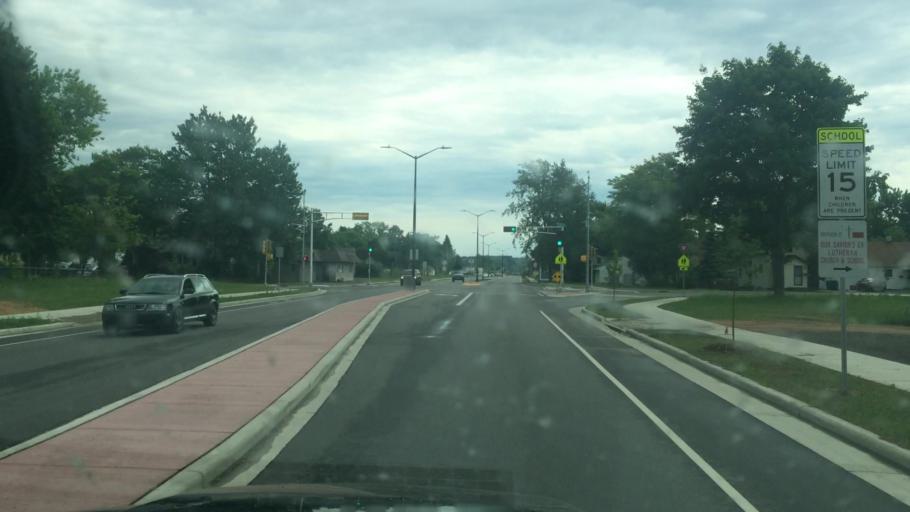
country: US
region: Wisconsin
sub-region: Marathon County
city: Wausau
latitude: 44.9483
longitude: -89.6500
